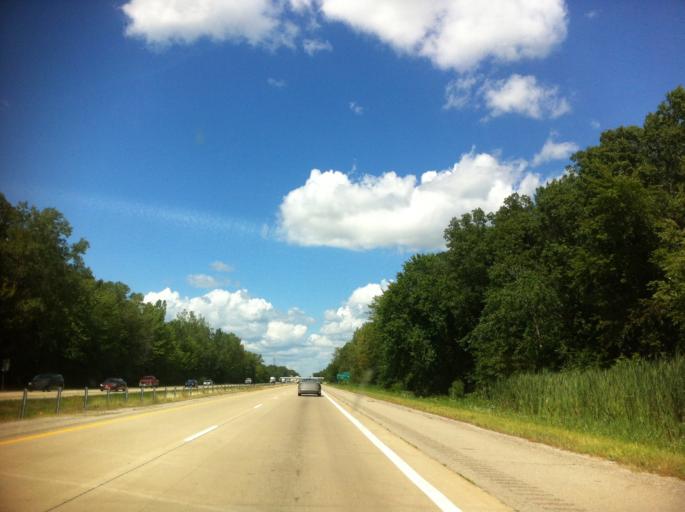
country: US
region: Michigan
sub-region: Monroe County
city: Petersburg
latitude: 41.9018
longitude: -83.6616
